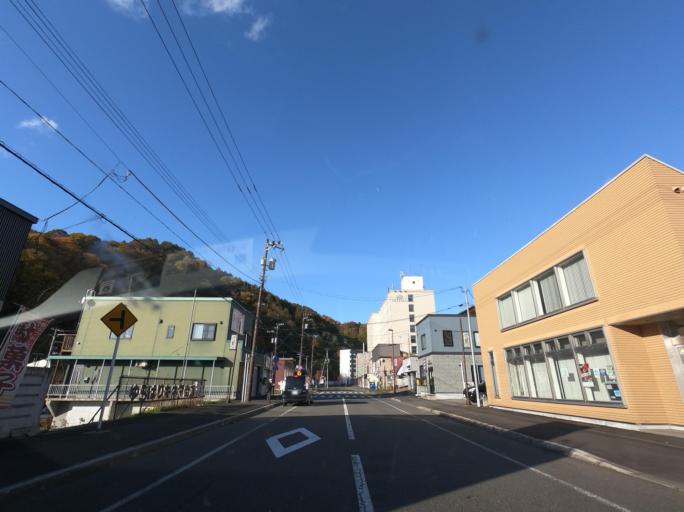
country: JP
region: Hokkaido
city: Iwamizawa
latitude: 43.0583
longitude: 141.9767
